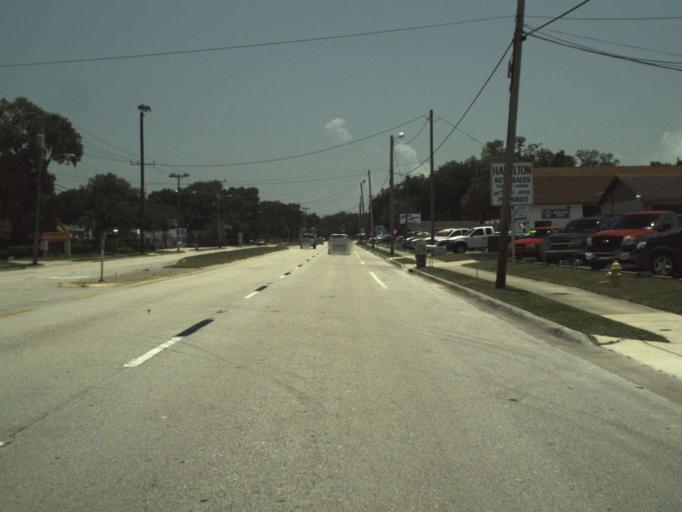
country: US
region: Florida
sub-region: Volusia County
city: Port Orange
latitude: 29.1177
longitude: -80.9751
